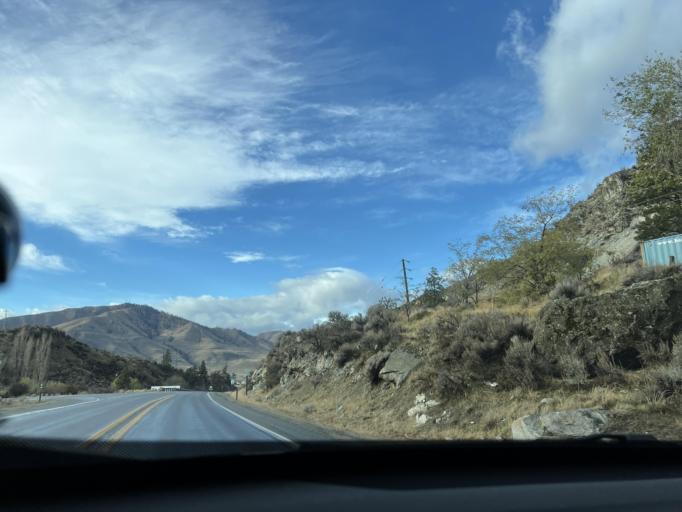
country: US
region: Washington
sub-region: Chelan County
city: Chelan
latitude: 47.8455
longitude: -119.9727
